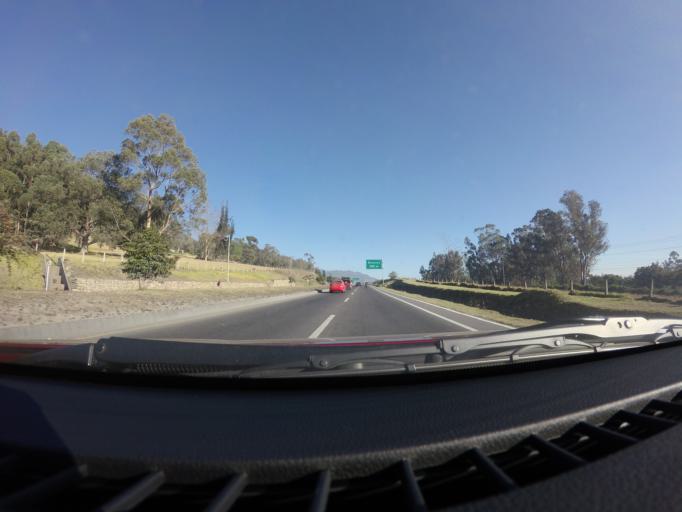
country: CO
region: Cundinamarca
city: Zipaquira
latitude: 4.9906
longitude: -74.0035
